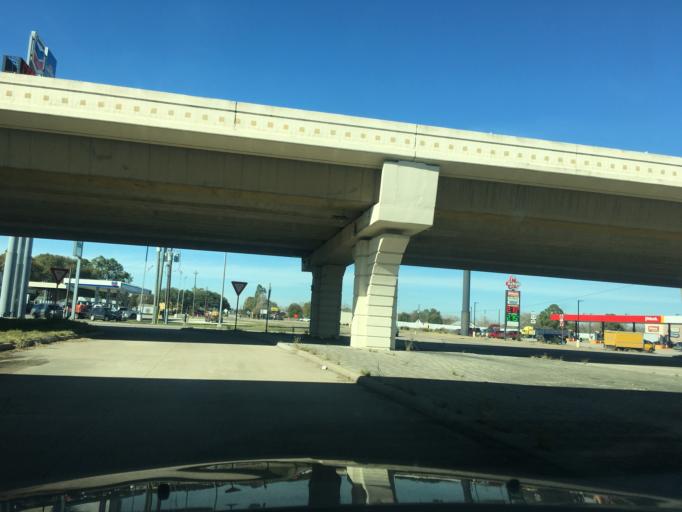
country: US
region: Texas
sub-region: Fort Bend County
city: Pleak
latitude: 29.4940
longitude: -95.9117
